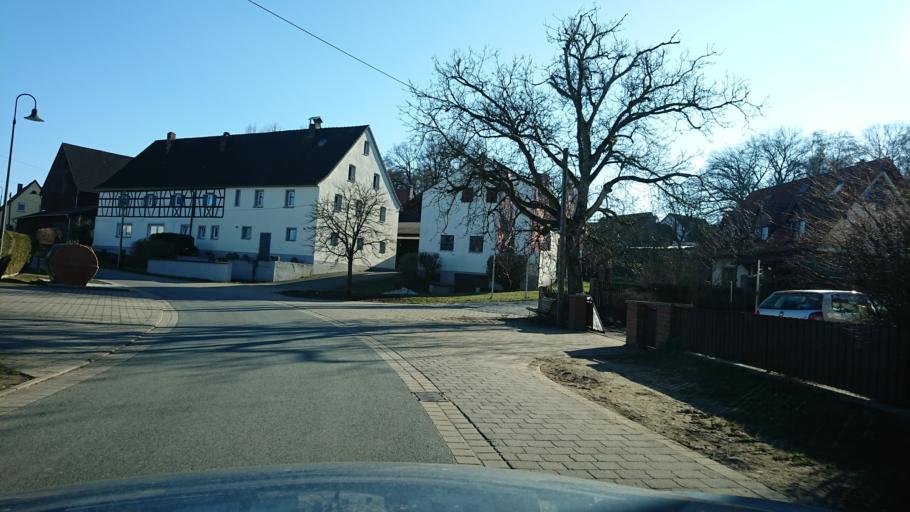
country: DE
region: Bavaria
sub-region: Upper Franconia
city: Neunkirchen am Brand
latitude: 49.6246
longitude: 11.1065
